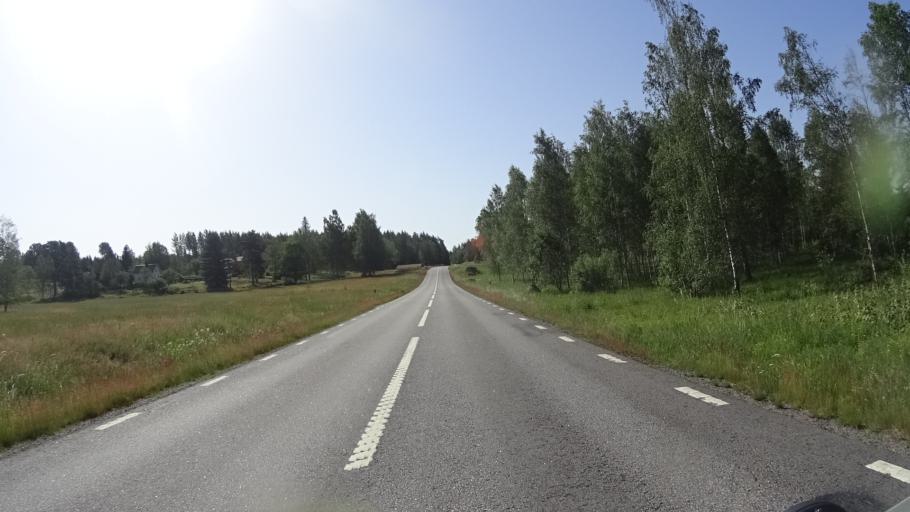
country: SE
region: OEstergoetland
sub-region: Atvidabergs Kommun
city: Atvidaberg
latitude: 58.0842
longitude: 16.1466
